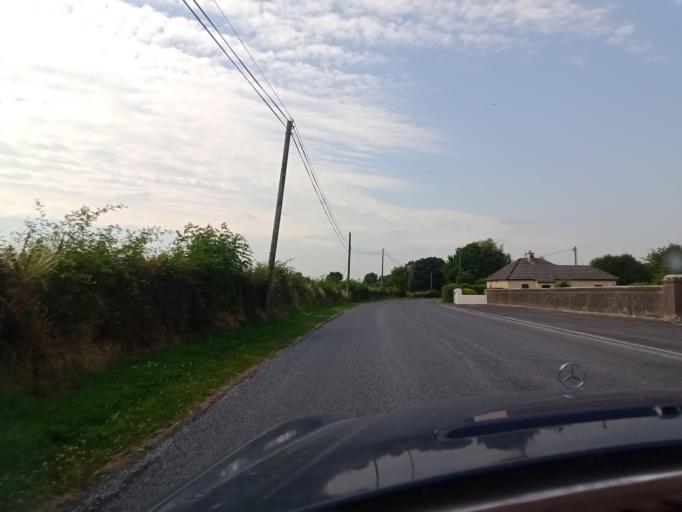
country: IE
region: Leinster
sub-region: Kilkenny
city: Callan
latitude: 52.4728
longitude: -7.3270
